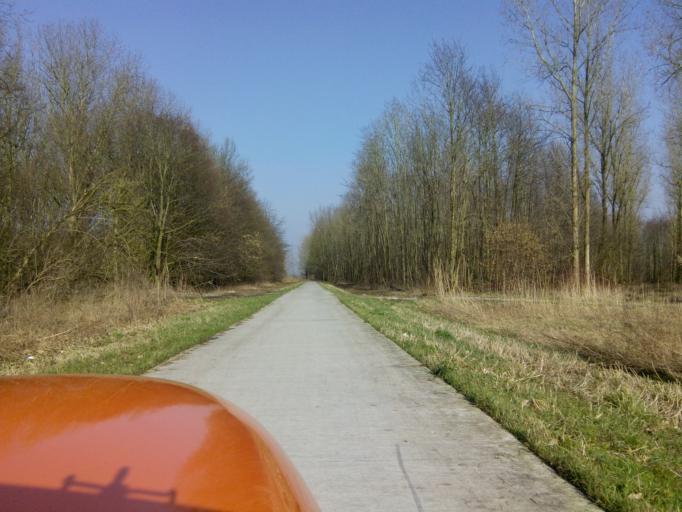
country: NL
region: Flevoland
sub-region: Gemeente Zeewolde
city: Zeewolde
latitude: 52.3450
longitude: 5.4740
